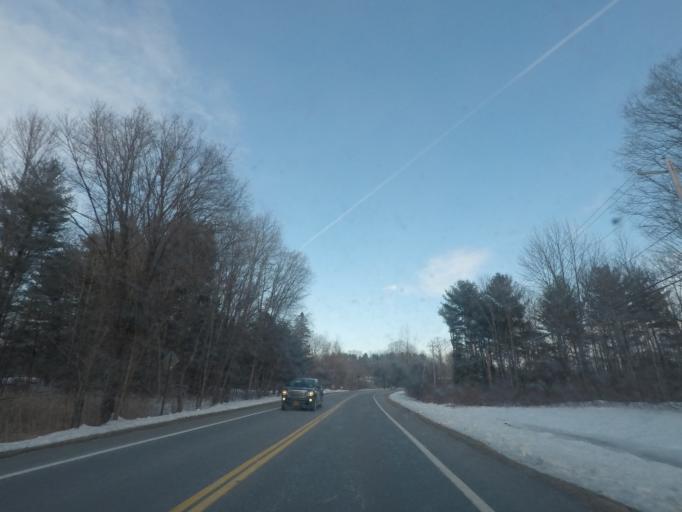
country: US
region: New York
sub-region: Schenectady County
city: Niskayuna
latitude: 42.8394
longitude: -73.8115
